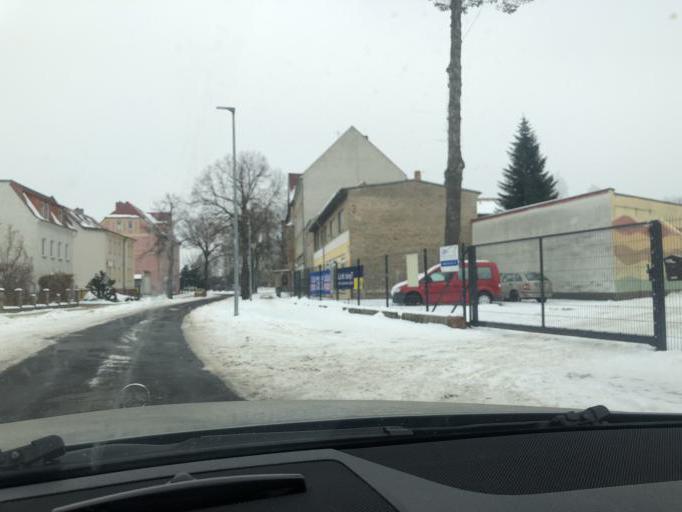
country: DE
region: Brandenburg
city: Guben
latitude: 51.9463
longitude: 14.7089
